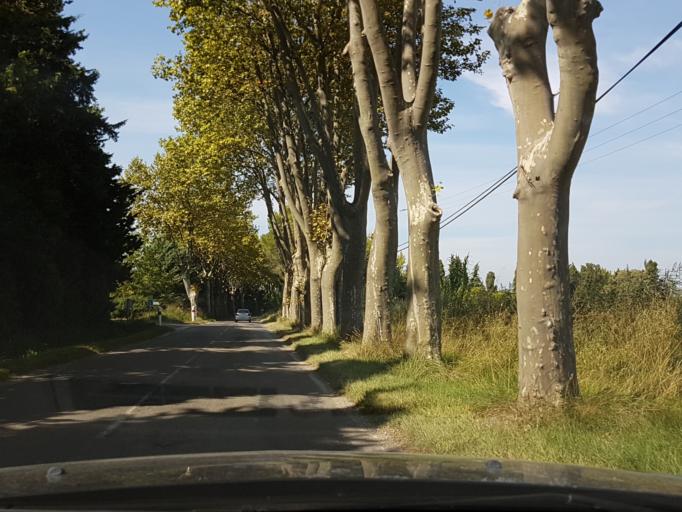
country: FR
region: Provence-Alpes-Cote d'Azur
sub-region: Departement des Bouches-du-Rhone
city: Eygalieres
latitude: 43.7777
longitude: 4.9296
